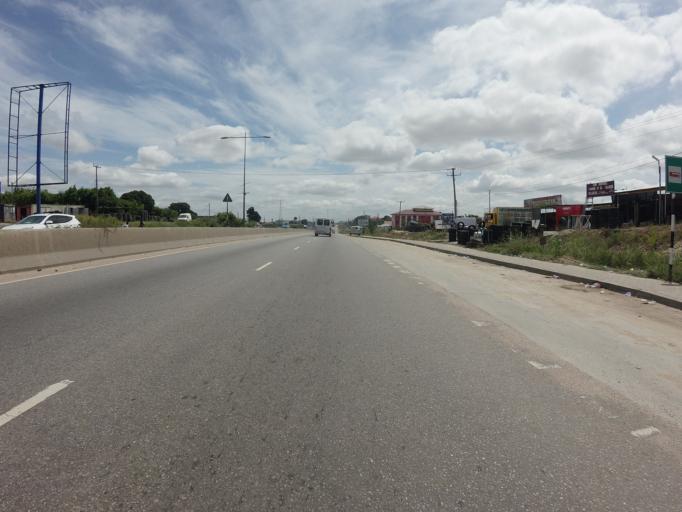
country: GH
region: Central
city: Kasoa
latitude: 5.5298
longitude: -0.4466
